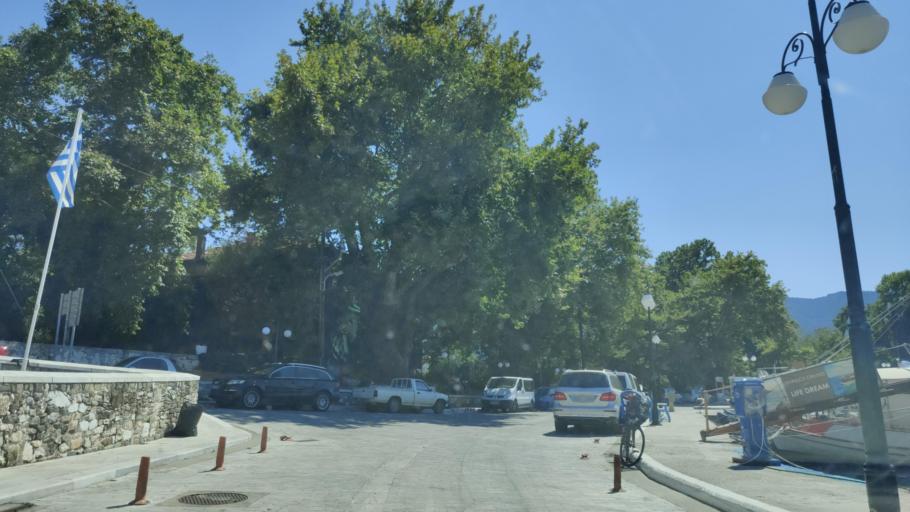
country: GR
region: East Macedonia and Thrace
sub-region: Nomos Kavalas
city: Thasos
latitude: 40.7811
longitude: 24.7135
